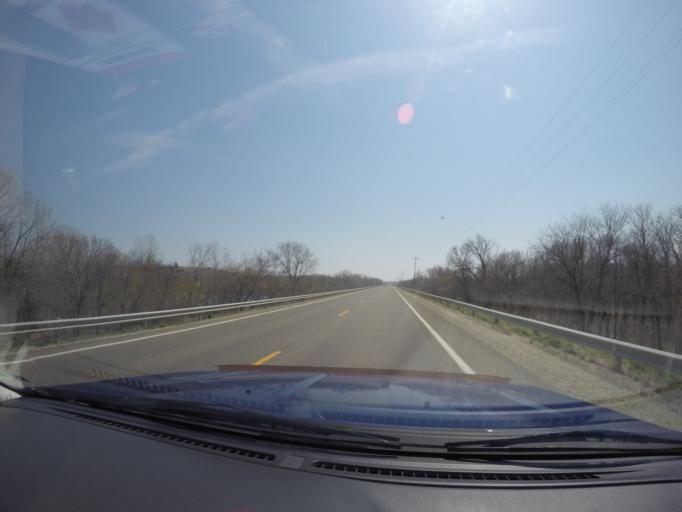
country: US
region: Kansas
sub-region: Morris County
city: Council Grove
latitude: 38.7334
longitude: -96.5004
